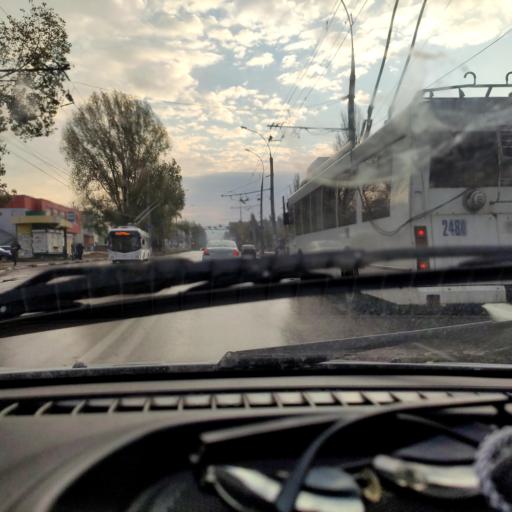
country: RU
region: Samara
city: Tol'yatti
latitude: 53.5365
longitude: 49.2959
